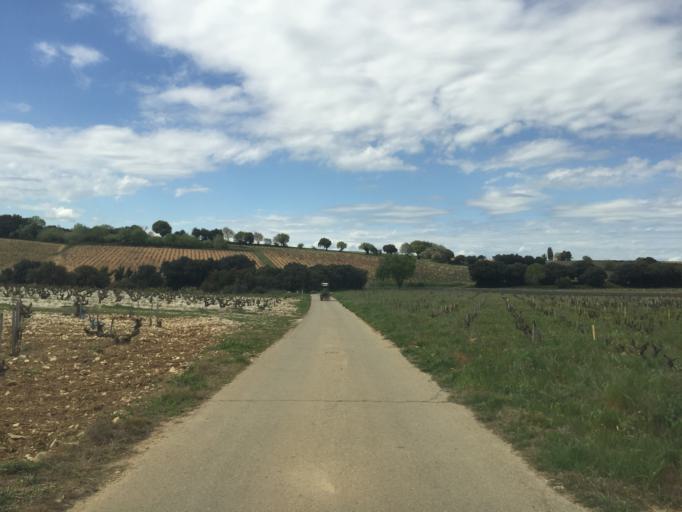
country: FR
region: Provence-Alpes-Cote d'Azur
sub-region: Departement du Vaucluse
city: Chateauneuf-du-Pape
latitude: 44.0757
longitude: 4.8276
